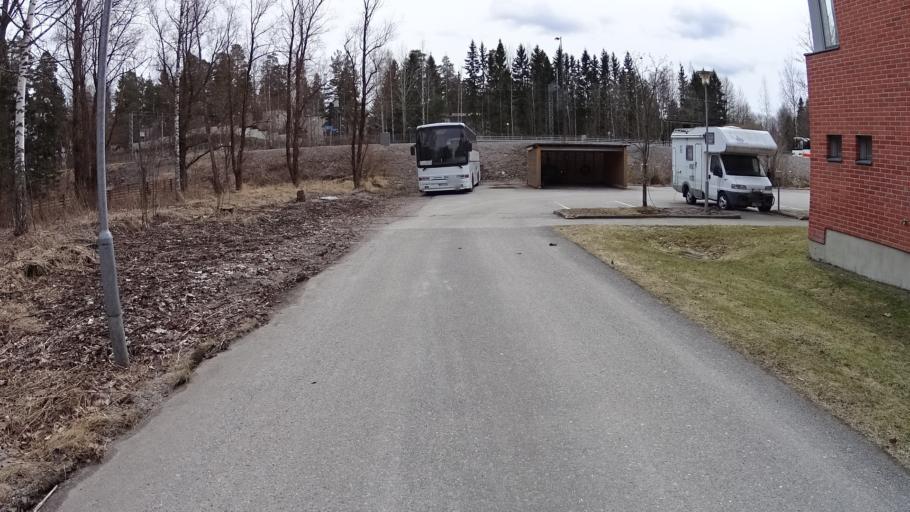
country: FI
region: Uusimaa
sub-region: Helsinki
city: Kauniainen
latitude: 60.2135
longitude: 24.7376
